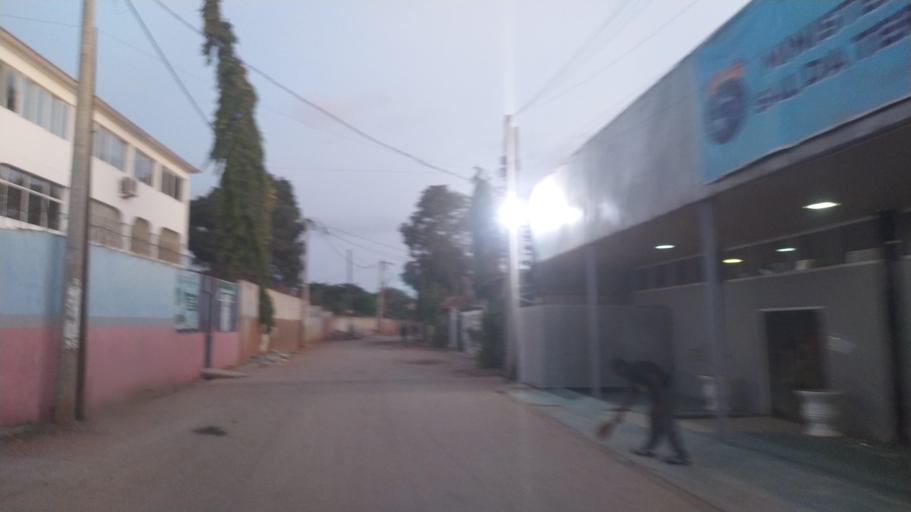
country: AO
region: Luanda
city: Luanda
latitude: -8.8978
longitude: 13.2045
